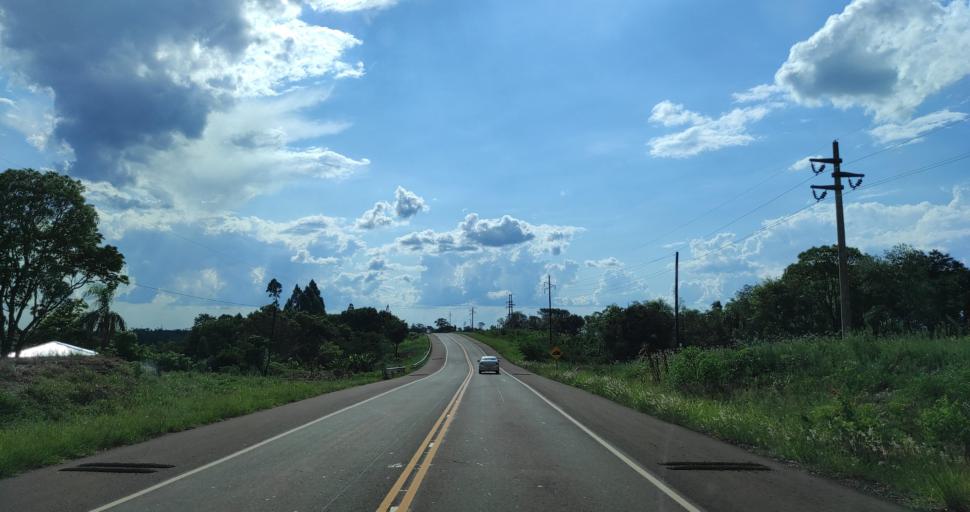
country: AR
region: Misiones
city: Bernardo de Irigoyen
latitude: -26.2988
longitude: -53.8063
